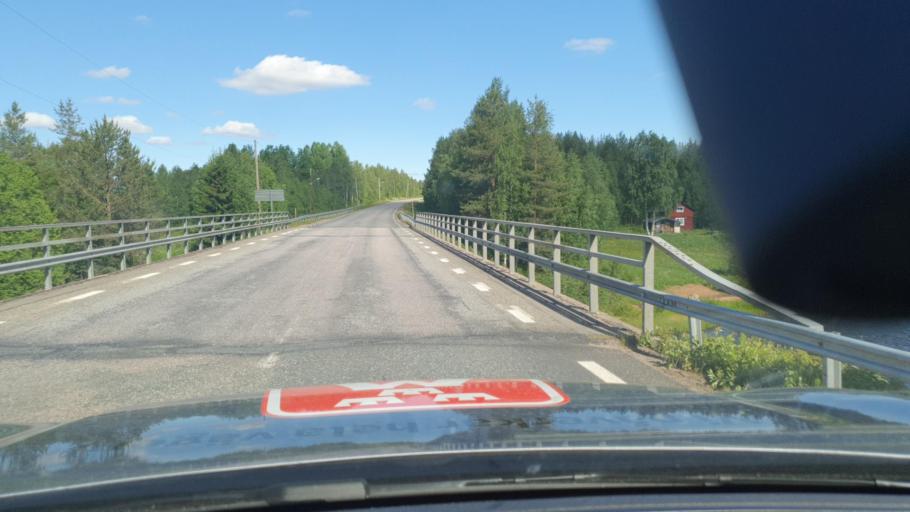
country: SE
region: Norrbotten
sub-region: Overkalix Kommun
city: OEverkalix
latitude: 66.9279
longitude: 22.7381
